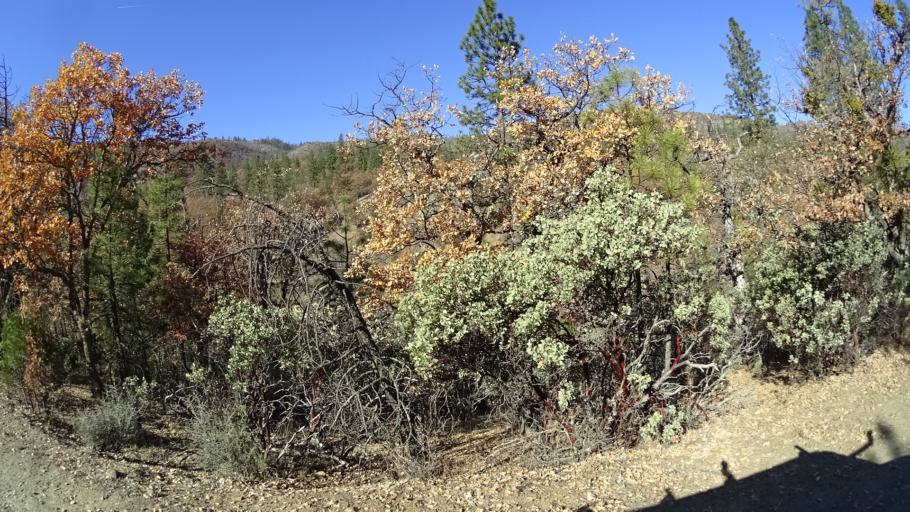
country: US
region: California
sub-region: Siskiyou County
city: Yreka
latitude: 41.8528
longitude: -122.8331
